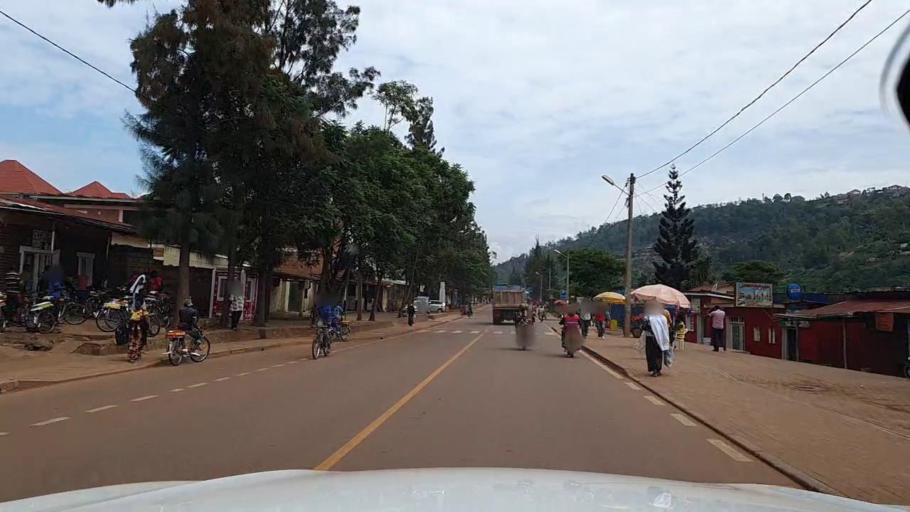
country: RW
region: Kigali
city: Kigali
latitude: -1.9227
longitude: 30.0468
